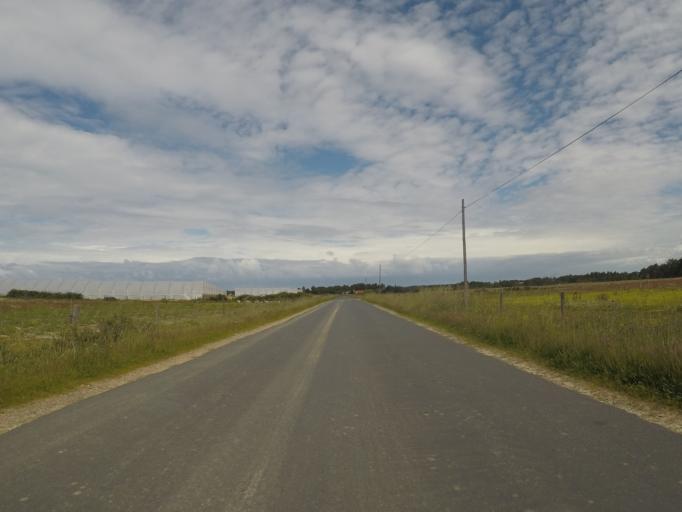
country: PT
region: Beja
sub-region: Odemira
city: Sao Teotonio
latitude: 37.4879
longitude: -8.7748
